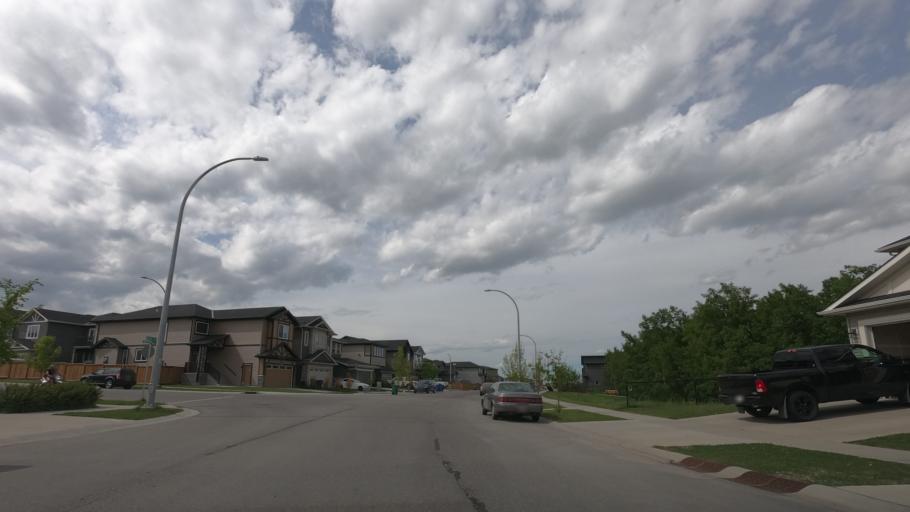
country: CA
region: Alberta
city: Airdrie
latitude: 51.2744
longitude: -114.0434
